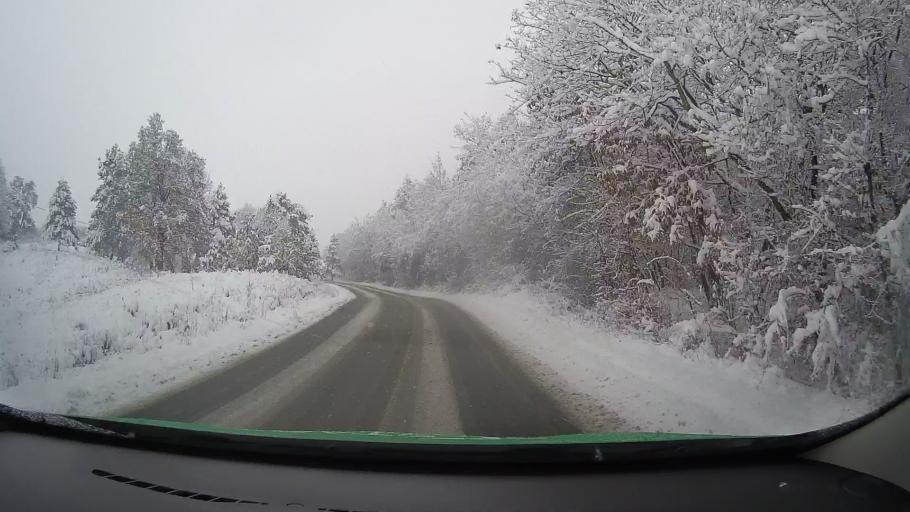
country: RO
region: Hunedoara
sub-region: Comuna Teliucu Inferior
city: Teliucu Inferior
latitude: 45.7064
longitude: 22.8820
